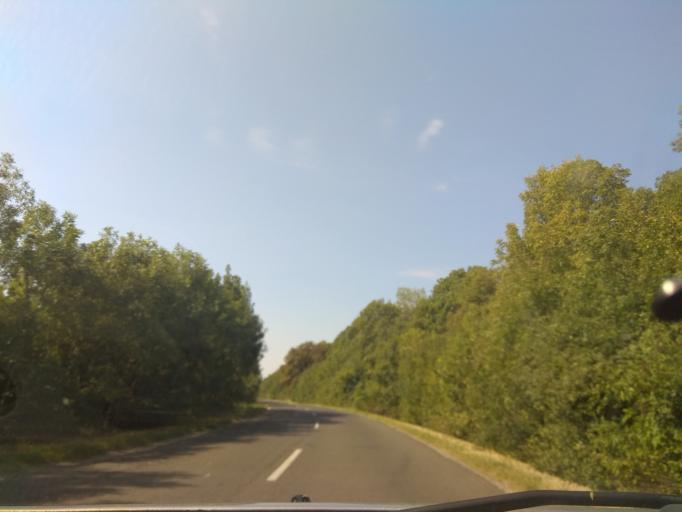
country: HU
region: Borsod-Abauj-Zemplen
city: Harsany
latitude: 47.9302
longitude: 20.7287
